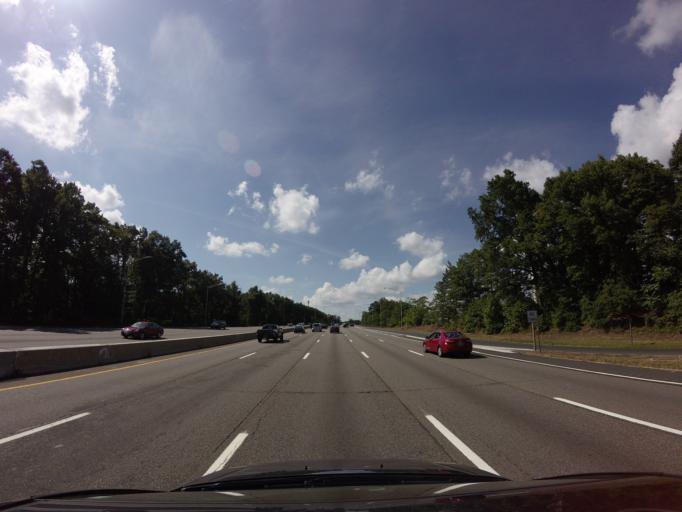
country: US
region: New Jersey
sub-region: Union County
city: Kenilworth
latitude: 40.6774
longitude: -74.2789
